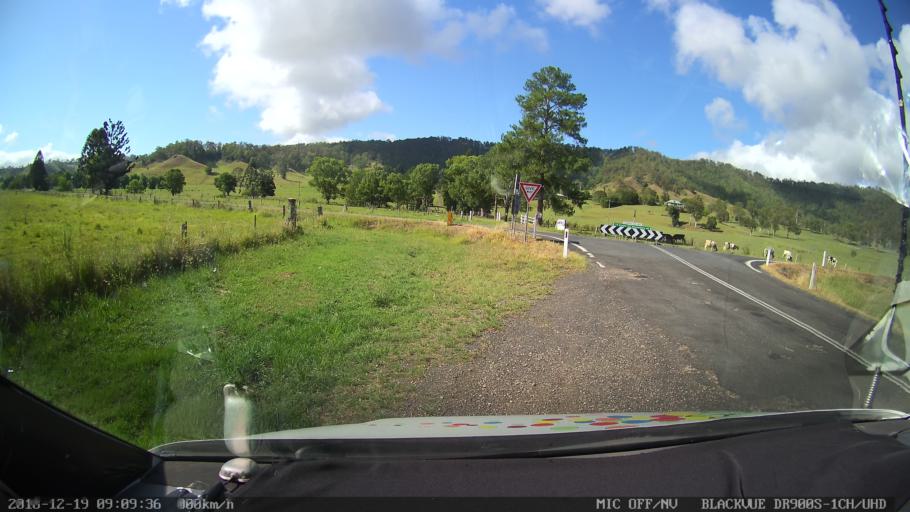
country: AU
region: New South Wales
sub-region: Kyogle
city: Kyogle
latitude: -28.4863
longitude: 152.9303
